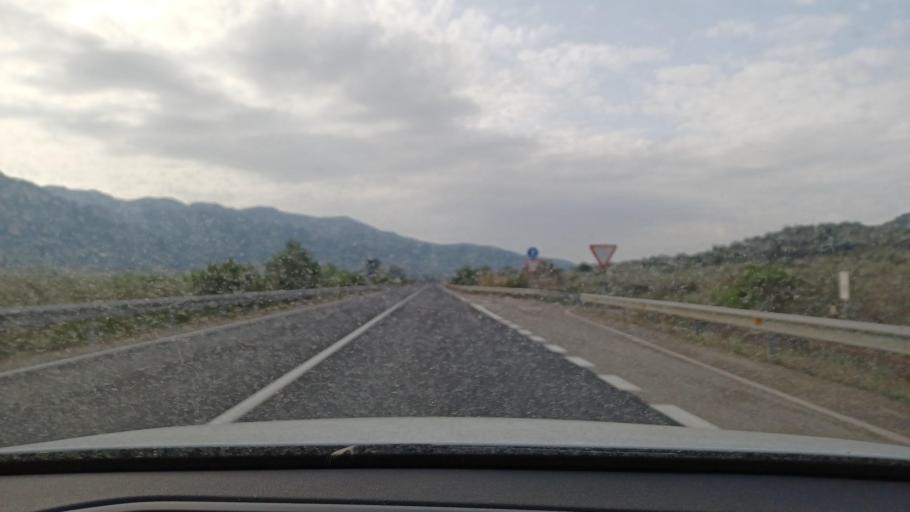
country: ES
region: Catalonia
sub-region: Provincia de Tarragona
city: Santa Barbara
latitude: 40.6633
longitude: 0.5074
